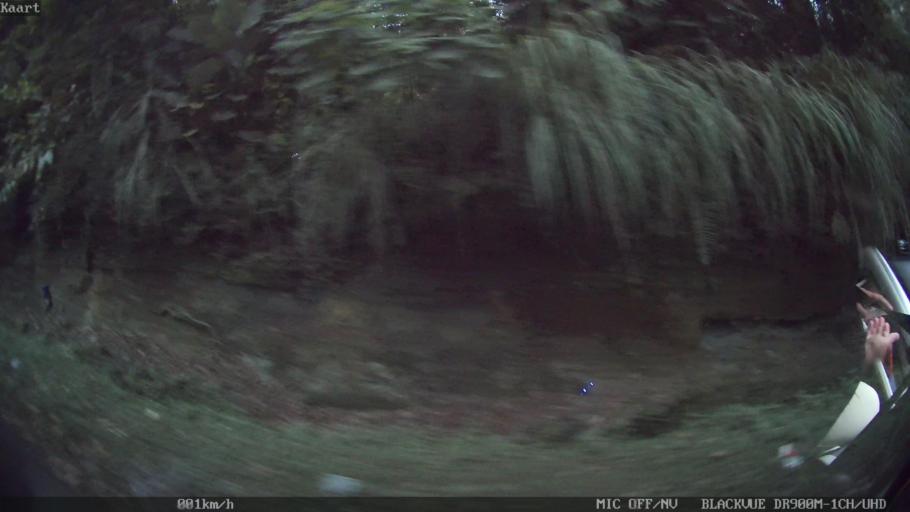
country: ID
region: Bali
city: Banjar Kedisan
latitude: -8.2612
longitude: 115.3351
